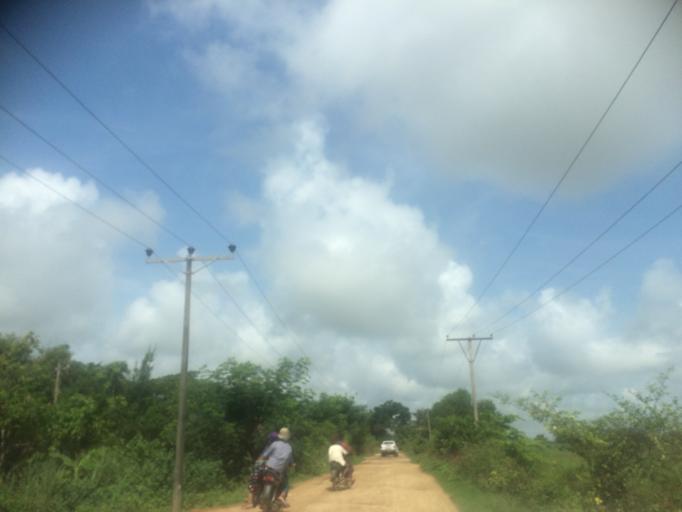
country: MM
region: Bago
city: Tharyarwady
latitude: 17.3119
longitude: 95.9157
